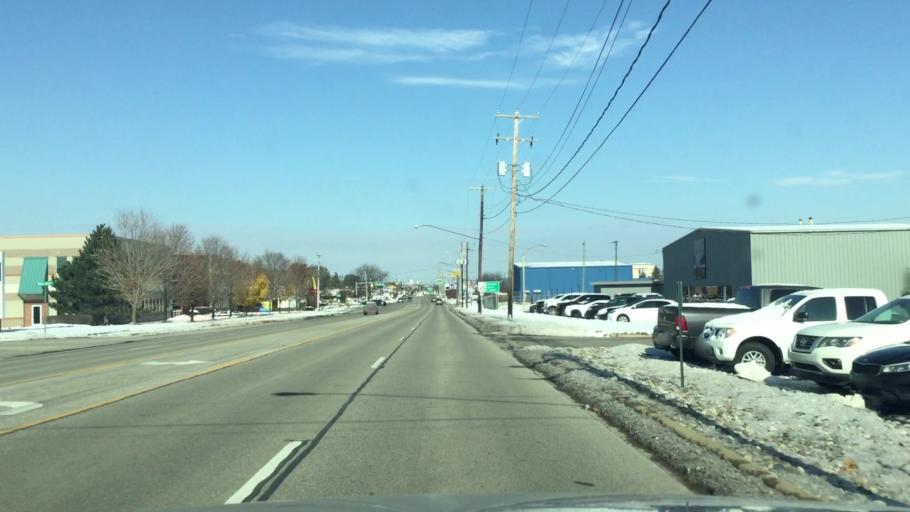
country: US
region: Michigan
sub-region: Kalamazoo County
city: Portage
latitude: 42.2357
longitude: -85.5601
